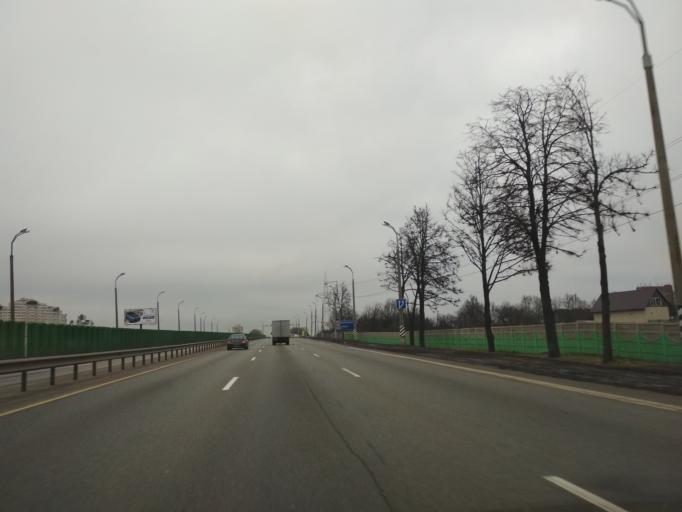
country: BY
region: Minsk
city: Shchomyslitsa
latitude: 53.8444
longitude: 27.4604
